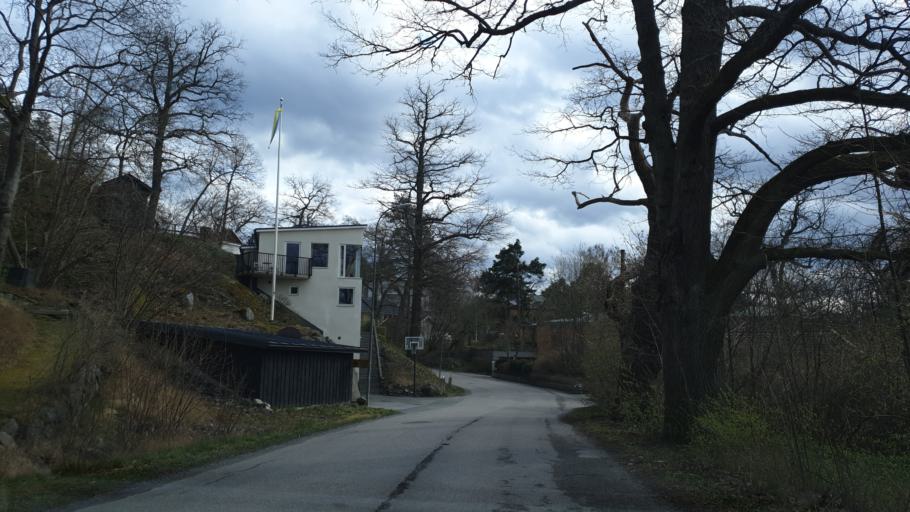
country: SE
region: Stockholm
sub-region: Nacka Kommun
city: Saltsjobaden
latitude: 59.2771
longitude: 18.3021
